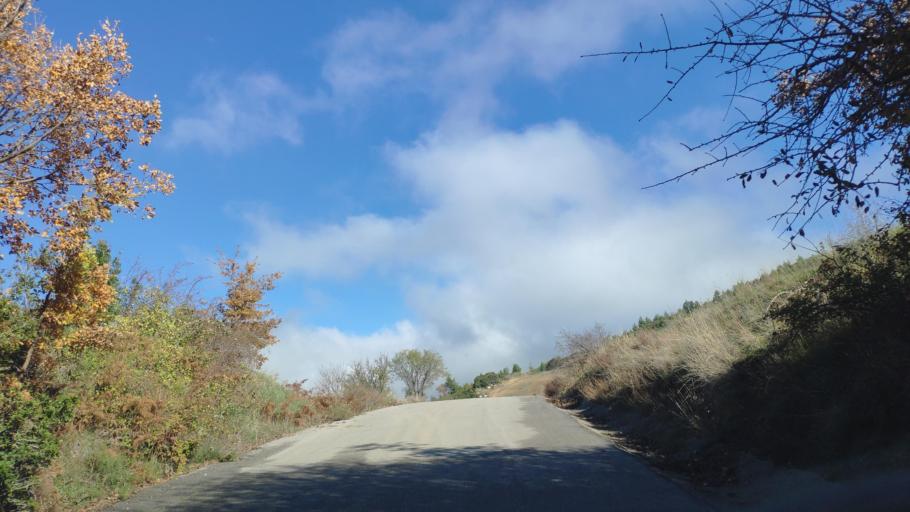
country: GR
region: West Greece
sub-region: Nomos Achaias
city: Aiyira
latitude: 38.0675
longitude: 22.4660
